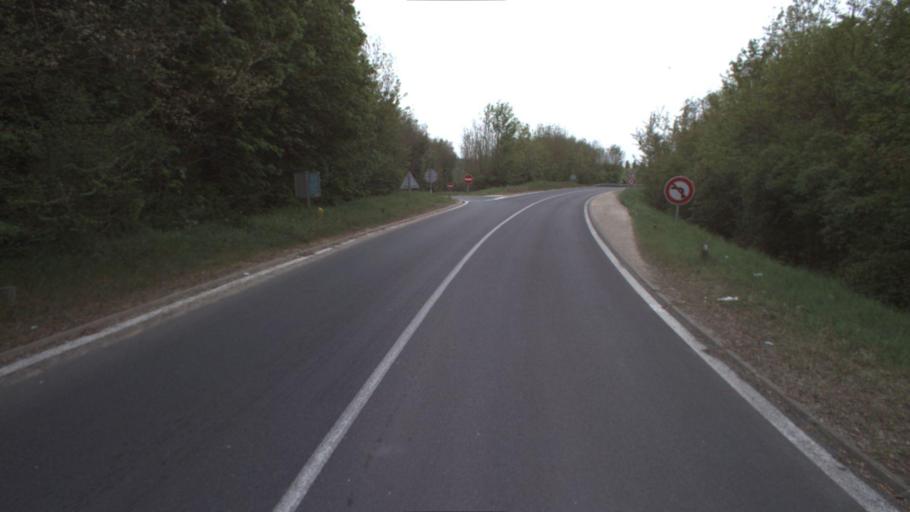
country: FR
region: Ile-de-France
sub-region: Departement de Seine-et-Marne
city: Lesigny
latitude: 48.7295
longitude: 2.6021
